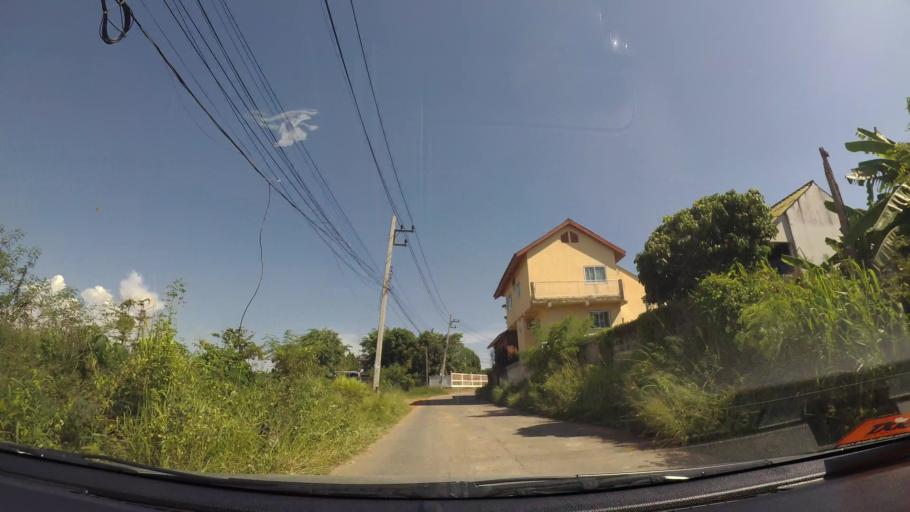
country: TH
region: Chon Buri
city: Si Racha
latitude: 13.1590
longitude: 100.9346
